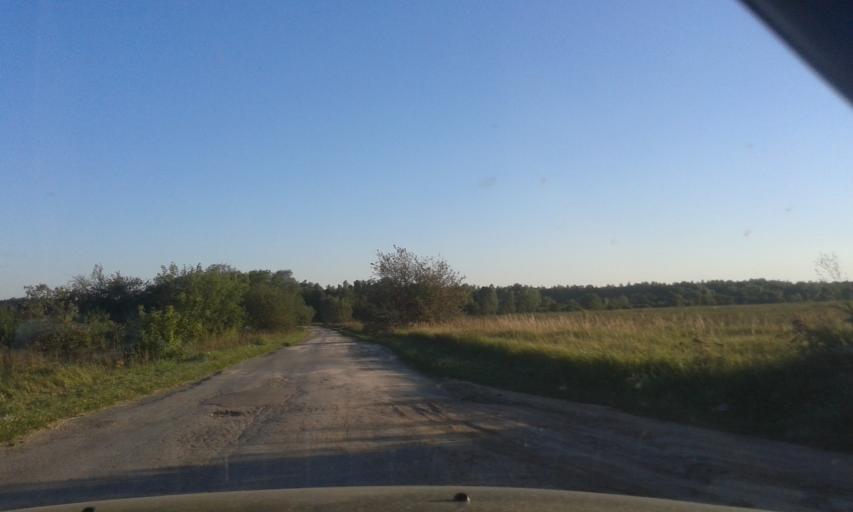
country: RU
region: Tula
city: Krapivna
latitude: 54.1234
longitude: 37.1539
